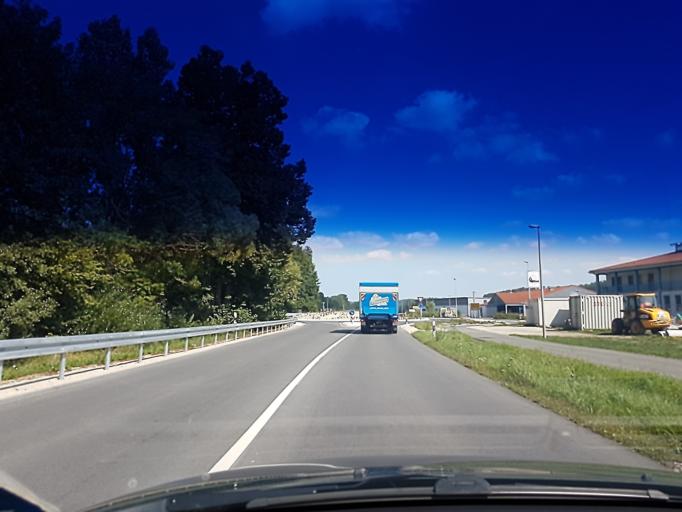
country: DE
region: Bavaria
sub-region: Upper Franconia
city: Weismain
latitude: 50.0926
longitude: 11.2383
